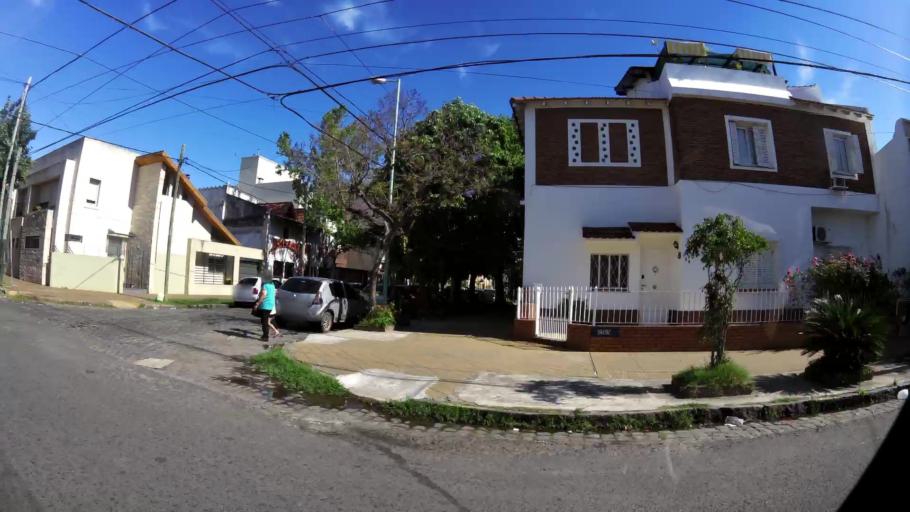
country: AR
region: Buenos Aires
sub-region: Partido de Lomas de Zamora
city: Lomas de Zamora
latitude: -34.7573
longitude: -58.4066
